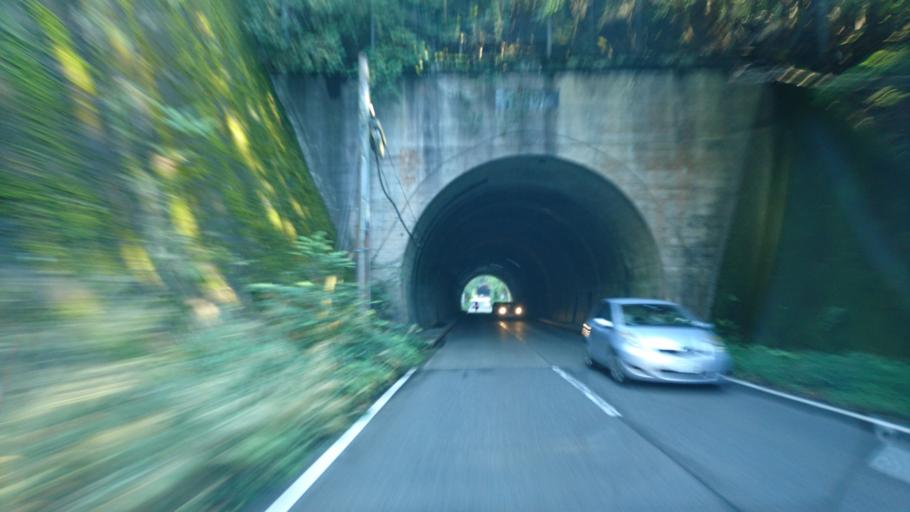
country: JP
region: Chiba
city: Kawaguchi
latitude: 35.1851
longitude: 140.0081
